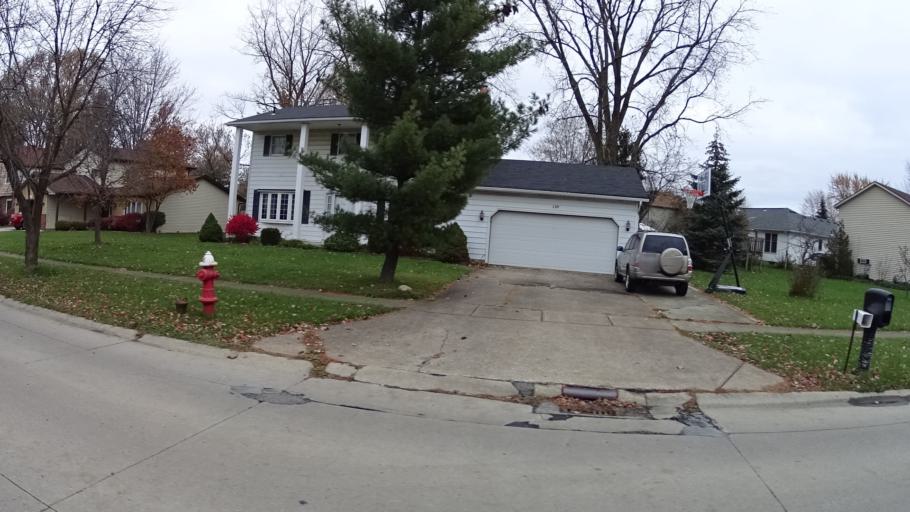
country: US
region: Ohio
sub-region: Lorain County
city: Sheffield
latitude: 41.4160
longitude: -82.0800
